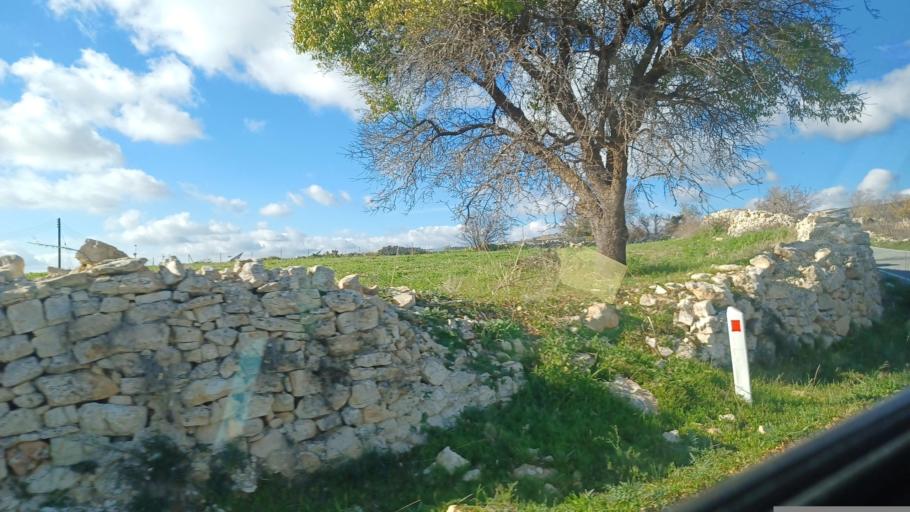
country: CY
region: Limassol
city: Pachna
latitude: 34.8349
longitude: 32.8000
